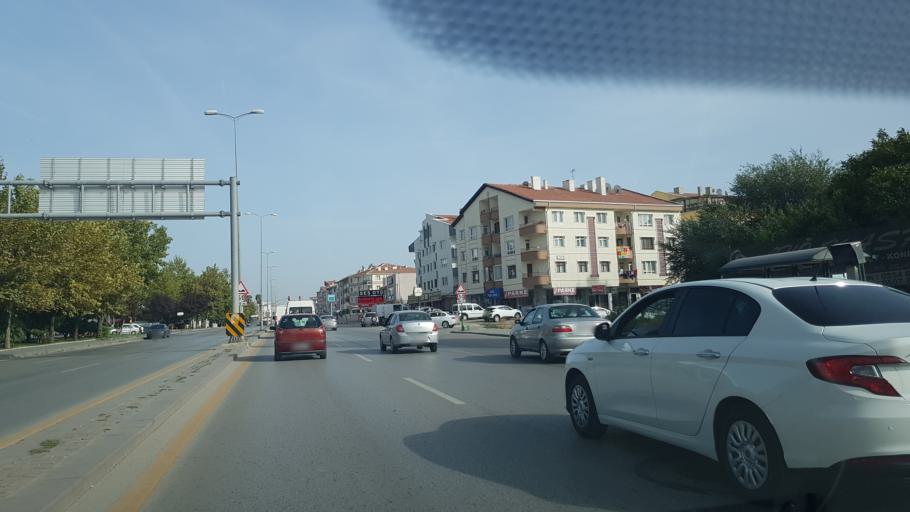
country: TR
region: Ankara
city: Etimesgut
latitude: 39.9554
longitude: 32.6289
